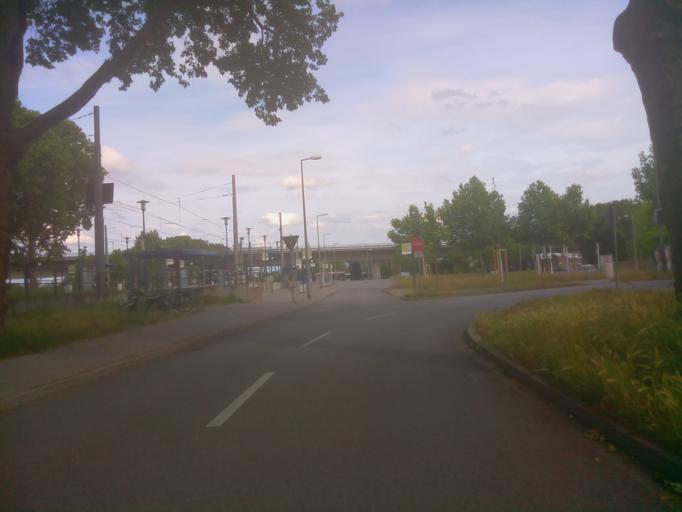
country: DE
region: Baden-Wuerttemberg
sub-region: Karlsruhe Region
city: Mannheim
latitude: 49.4779
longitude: 8.5214
